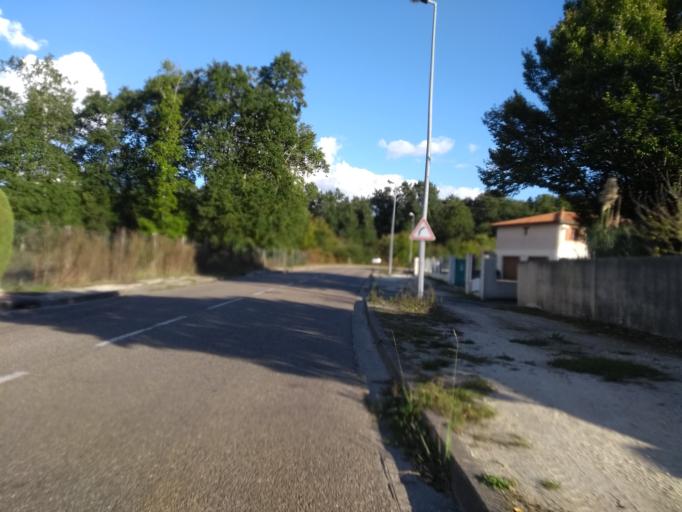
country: FR
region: Aquitaine
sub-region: Departement de la Gironde
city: Canejan
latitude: 44.7474
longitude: -0.6387
